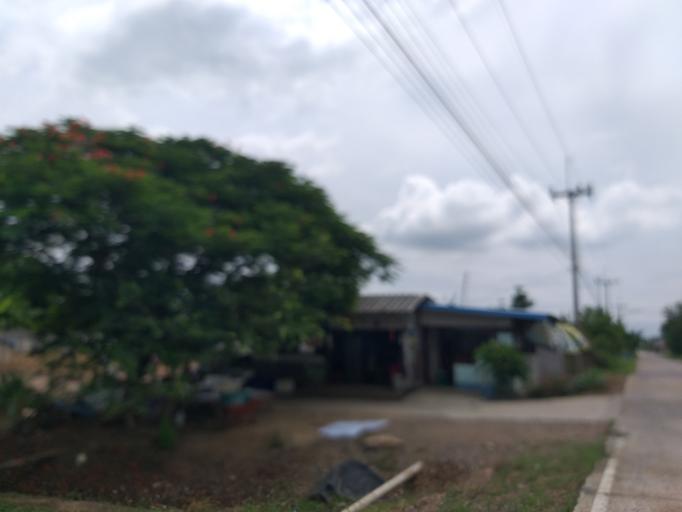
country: TH
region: Pathum Thani
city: Ban Lam Luk Ka
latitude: 13.9829
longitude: 100.8544
